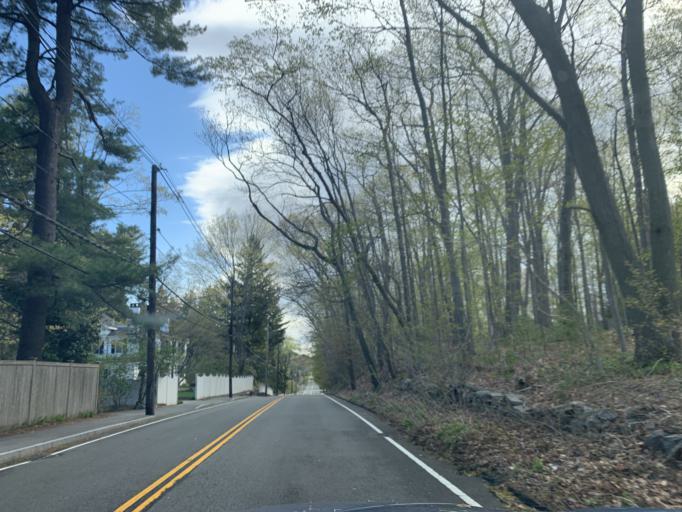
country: US
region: Massachusetts
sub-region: Norfolk County
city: Milton
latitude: 42.2395
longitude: -71.1036
